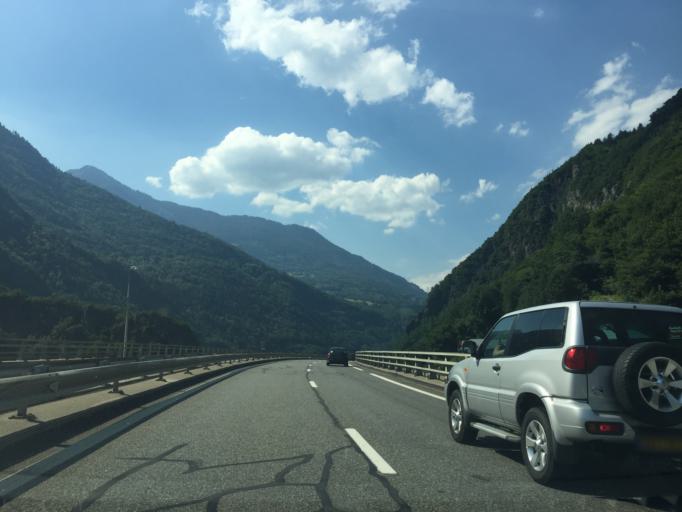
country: FR
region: Rhone-Alpes
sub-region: Departement de la Savoie
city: Aigueblanche
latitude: 45.5310
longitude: 6.4762
